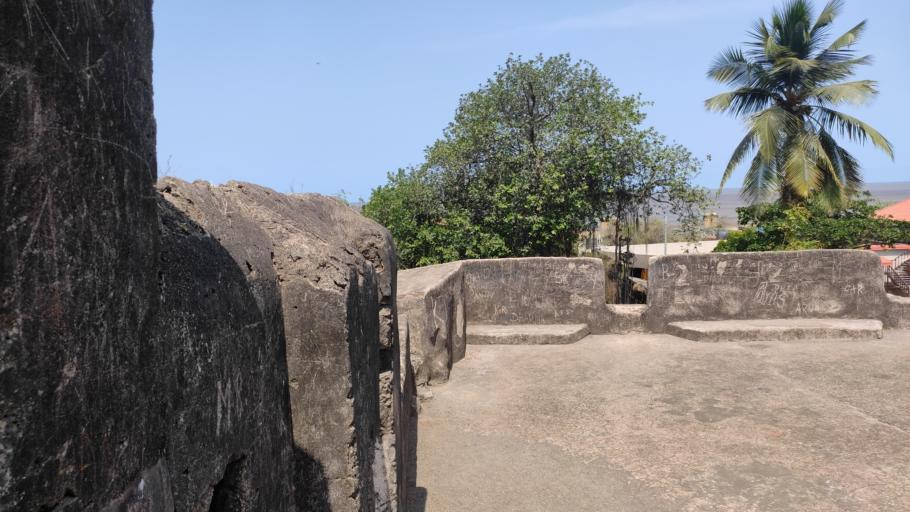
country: IN
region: Daman and Diu
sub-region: Daman District
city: Daman
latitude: 20.4137
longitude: 72.8317
